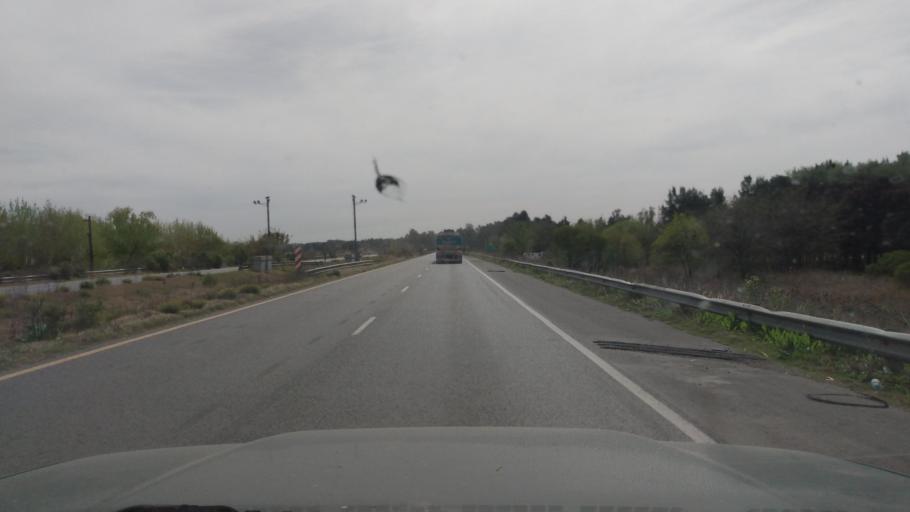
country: AR
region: Buenos Aires
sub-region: Partido de Lujan
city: Lujan
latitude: -34.5228
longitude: -59.0375
